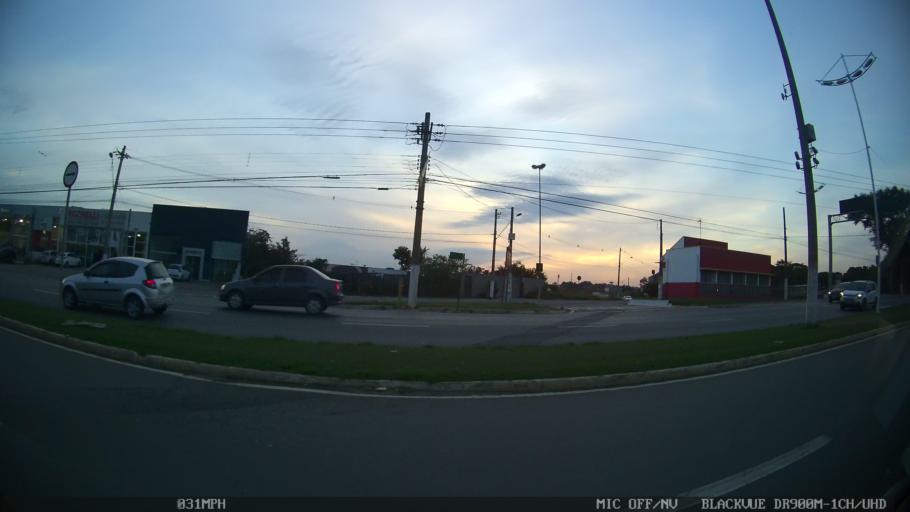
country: BR
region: Sao Paulo
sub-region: Limeira
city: Limeira
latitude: -22.5498
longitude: -47.3787
